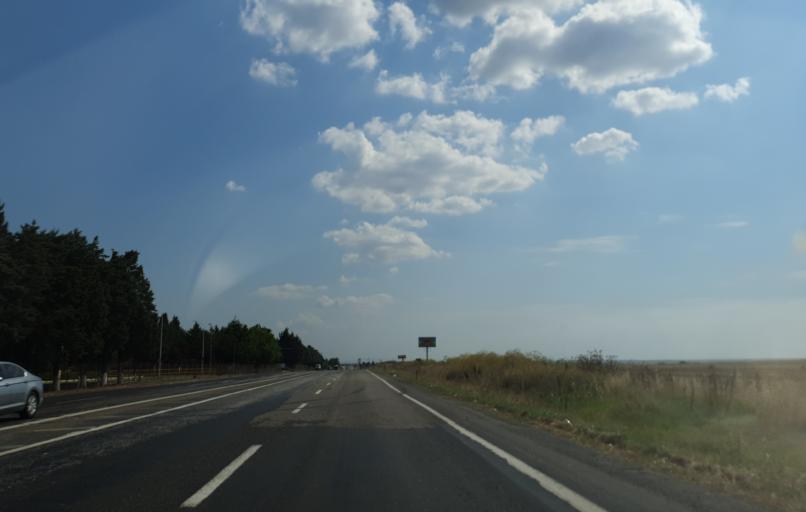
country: TR
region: Kirklareli
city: Buyukkaristiran
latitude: 41.2813
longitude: 27.5570
